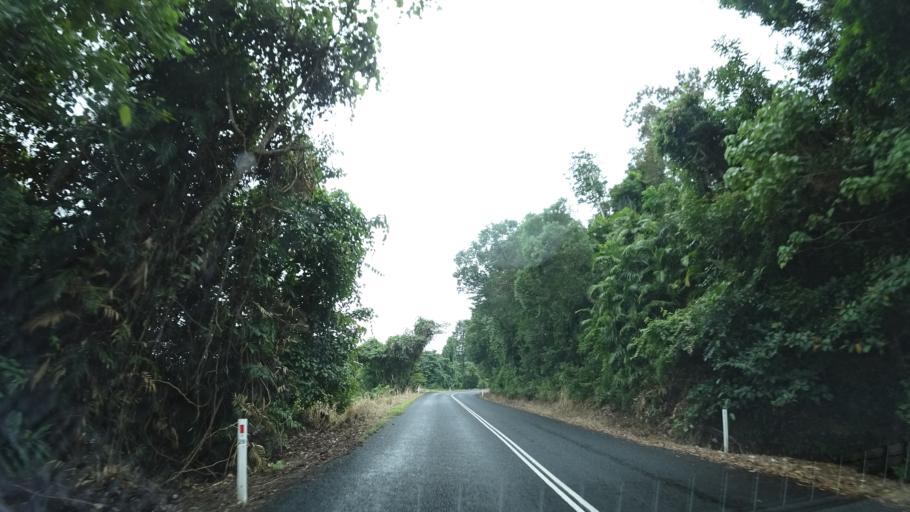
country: AU
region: Queensland
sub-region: Cassowary Coast
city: Innisfail
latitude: -17.5592
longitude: 146.0864
